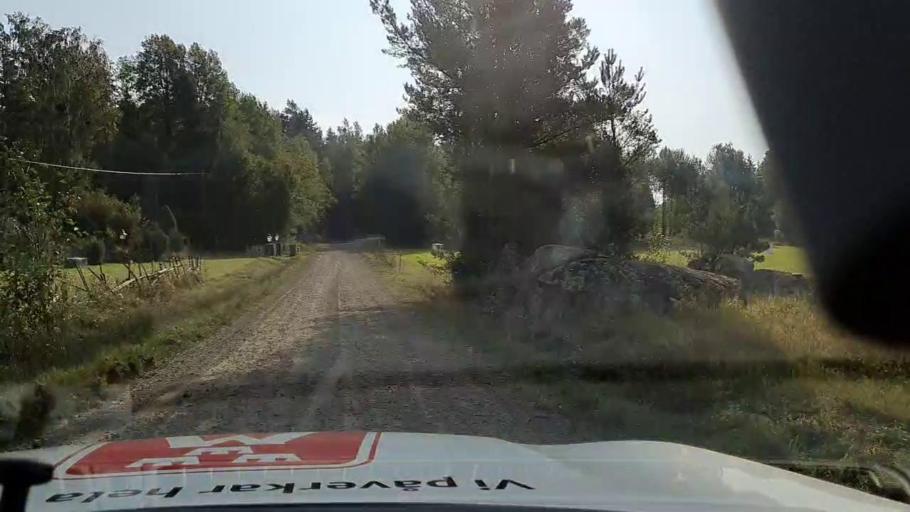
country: SE
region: Vaestmanland
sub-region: Kungsors Kommun
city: Kungsoer
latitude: 59.3490
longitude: 16.1665
